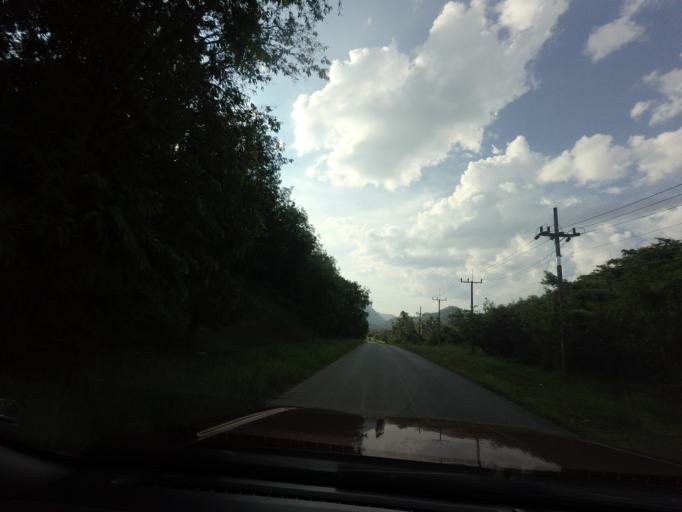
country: TH
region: Yala
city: Ban Nang Sata
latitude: 6.2175
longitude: 101.2313
